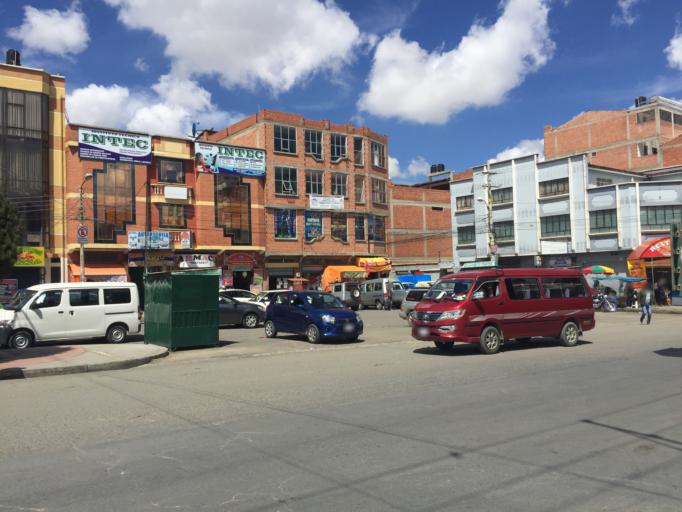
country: BO
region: La Paz
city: La Paz
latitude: -16.5218
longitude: -68.2103
